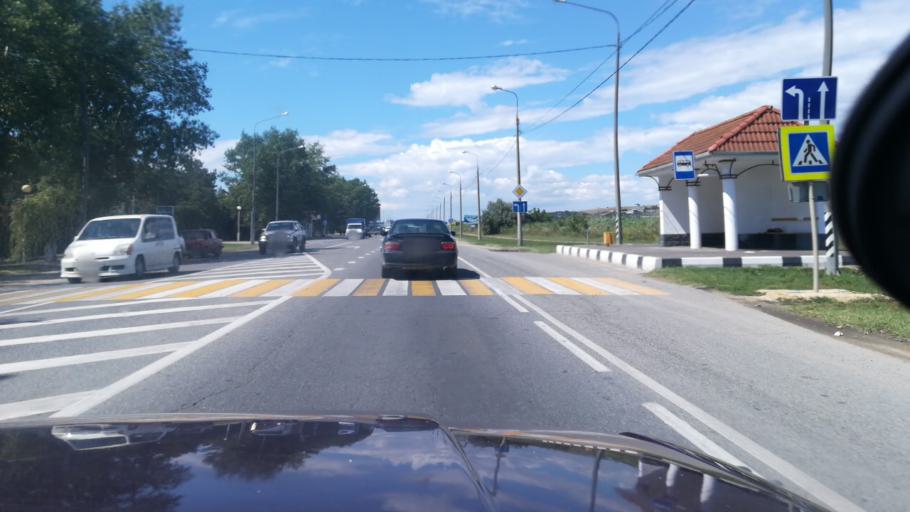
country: RU
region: Krasnodarskiy
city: Anapa
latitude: 44.9326
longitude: 37.3218
